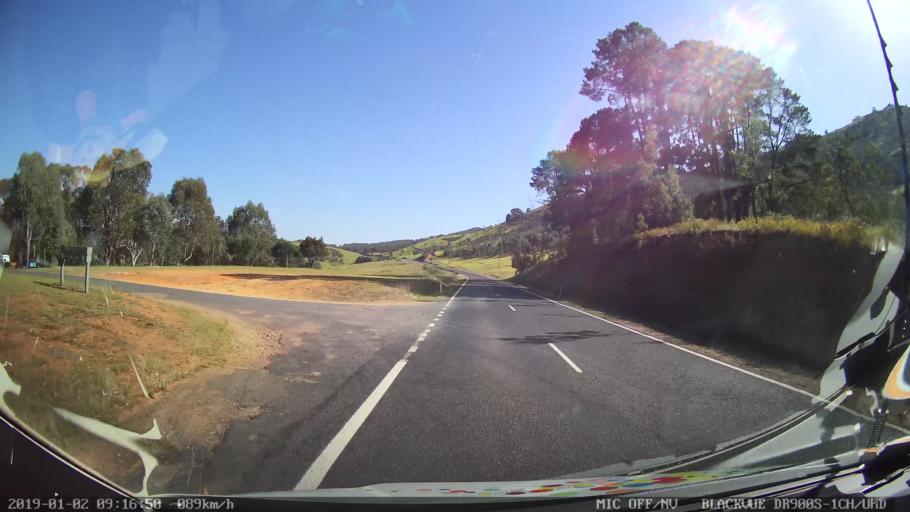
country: AU
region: New South Wales
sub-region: Tumut Shire
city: Tumut
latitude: -35.4487
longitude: 148.2854
